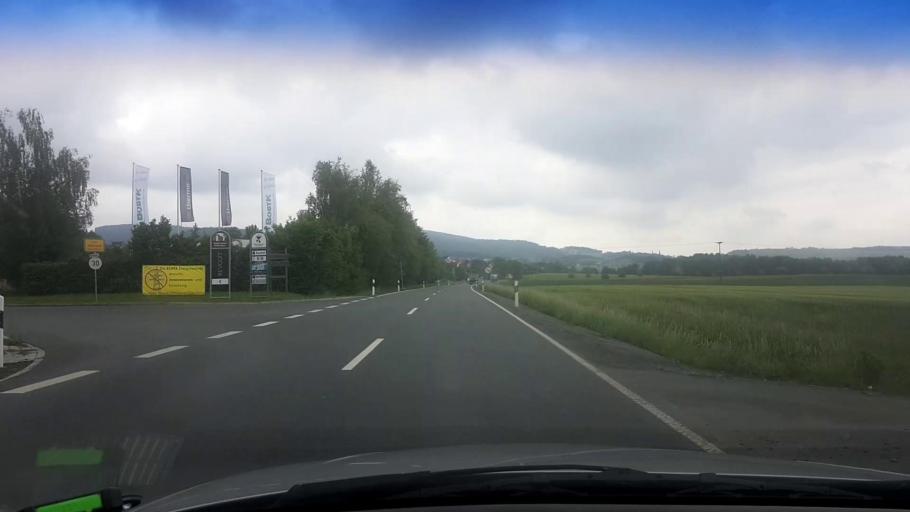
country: DE
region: Bavaria
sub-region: Upper Franconia
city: Goldkronach
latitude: 50.0118
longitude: 11.6731
